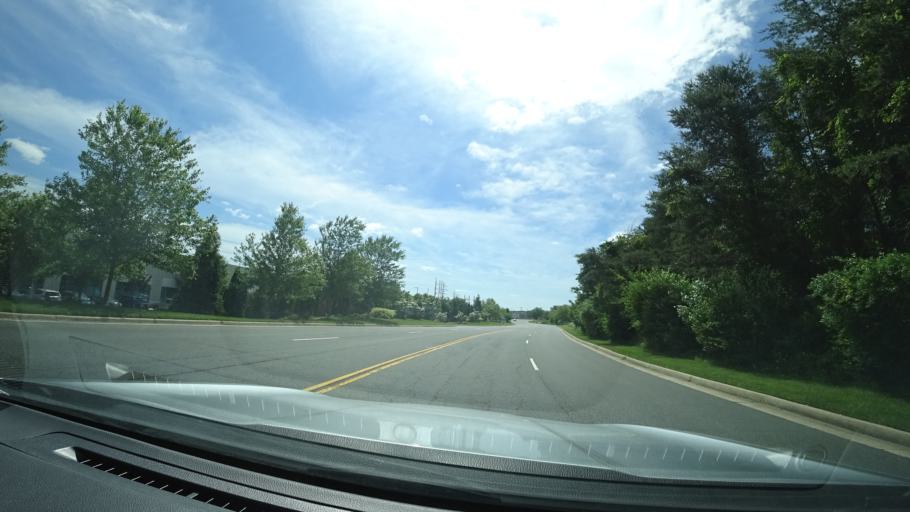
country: US
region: Virginia
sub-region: Loudoun County
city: Sterling
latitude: 38.9967
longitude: -77.4247
